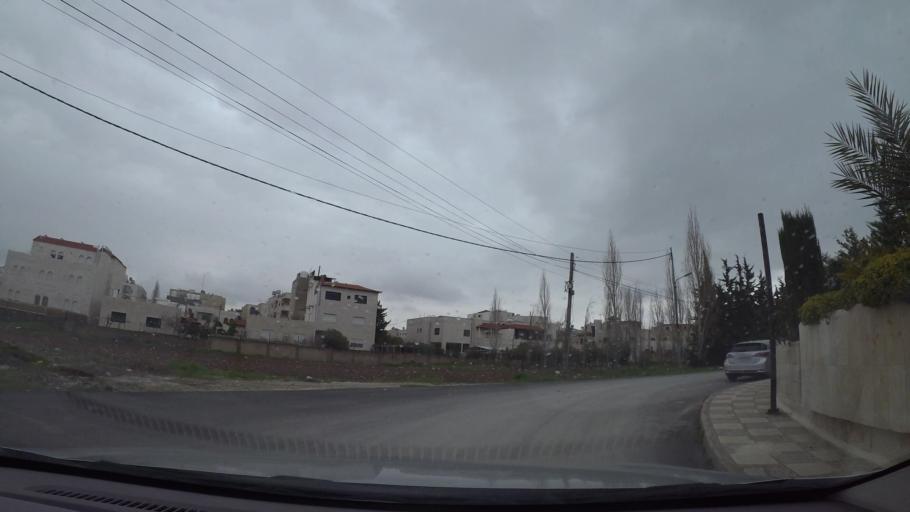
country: JO
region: Amman
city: Al Jubayhah
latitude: 31.9926
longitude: 35.8443
